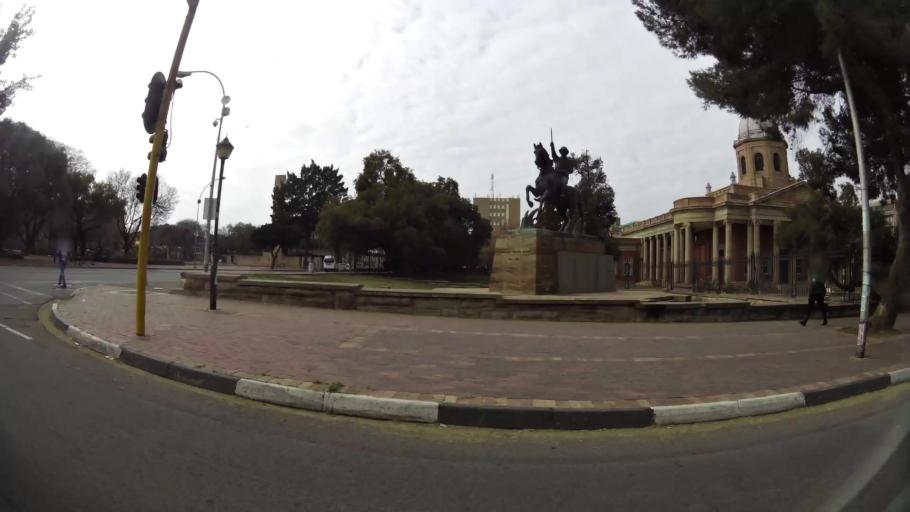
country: ZA
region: Orange Free State
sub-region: Mangaung Metropolitan Municipality
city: Bloemfontein
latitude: -29.1152
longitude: 26.2172
